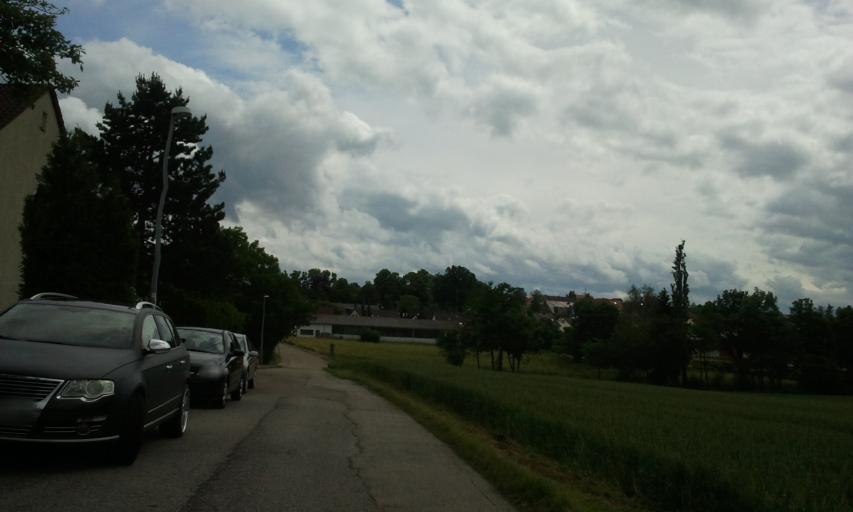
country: DE
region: Baden-Wuerttemberg
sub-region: Regierungsbezirk Stuttgart
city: Vaihingen an der Enz
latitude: 48.9553
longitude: 8.9735
